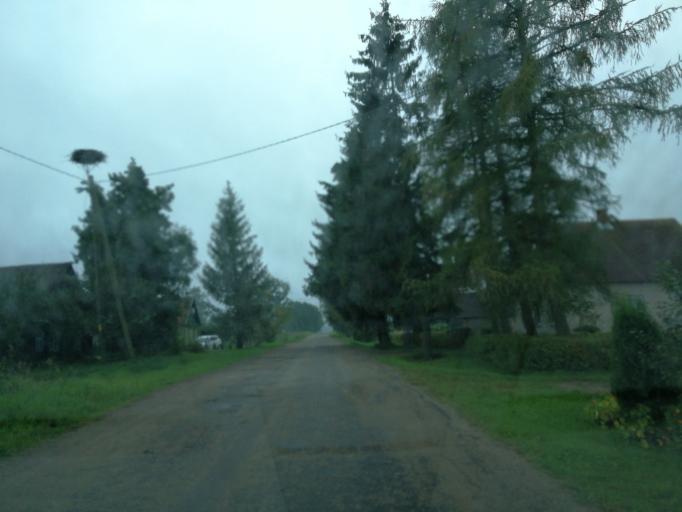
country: LV
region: Preilu Rajons
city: Jaunaglona
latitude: 56.3558
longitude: 26.9998
